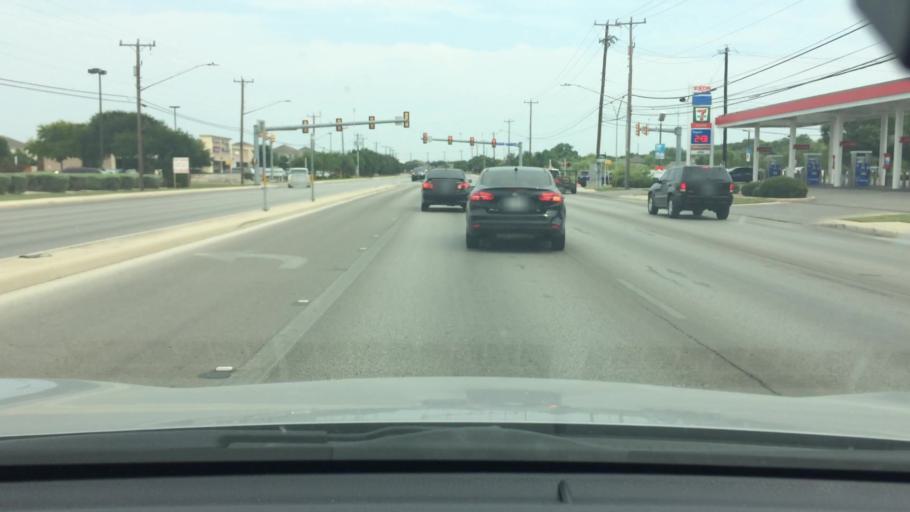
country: US
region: Texas
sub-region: Bexar County
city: Leon Valley
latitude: 29.4786
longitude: -98.6644
